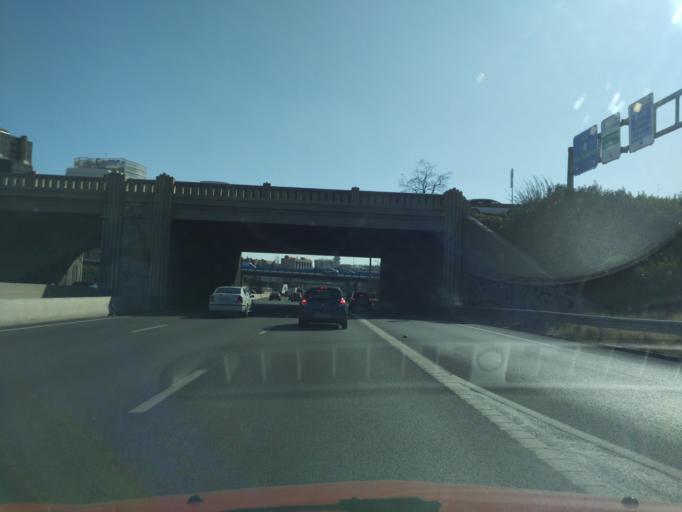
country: ES
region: Madrid
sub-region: Provincia de Madrid
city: Ciudad Lineal
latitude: 40.4450
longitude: -3.6612
